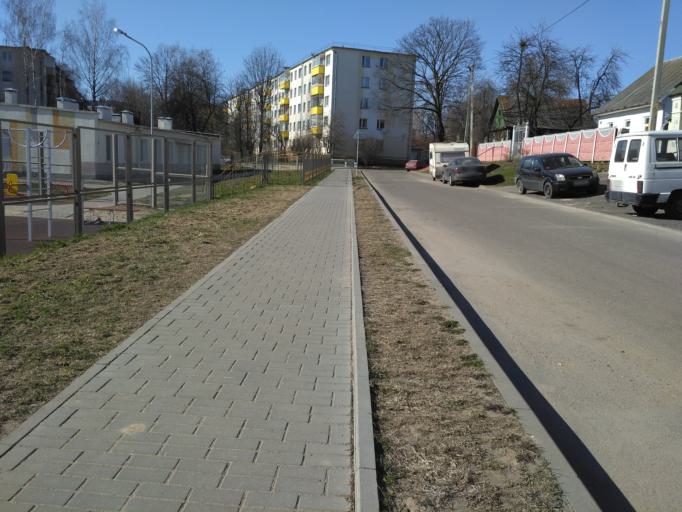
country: BY
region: Minsk
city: Minsk
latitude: 53.9025
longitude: 27.5098
